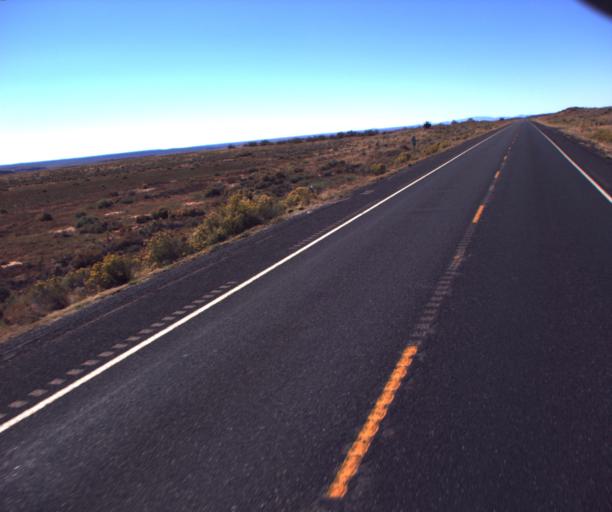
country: US
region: Arizona
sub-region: Coconino County
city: Fredonia
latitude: 36.9377
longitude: -112.5516
